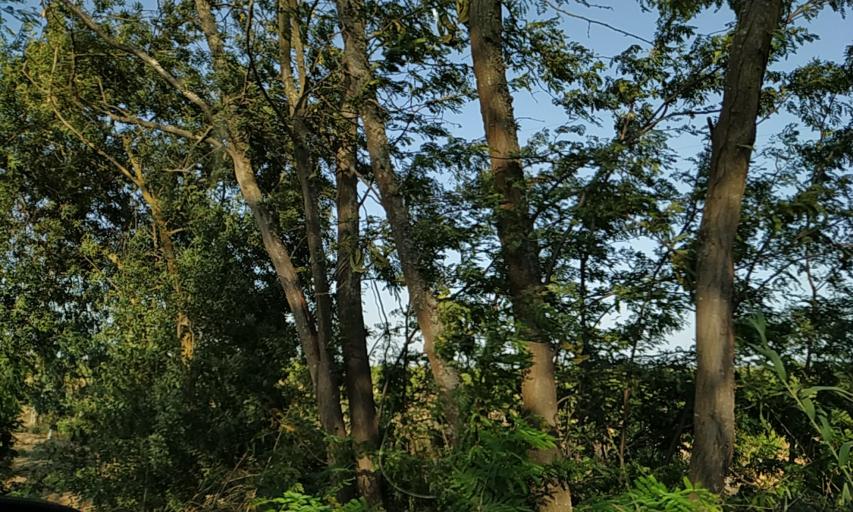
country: PT
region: Santarem
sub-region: Santarem
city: Santarem
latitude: 39.2687
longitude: -8.6625
